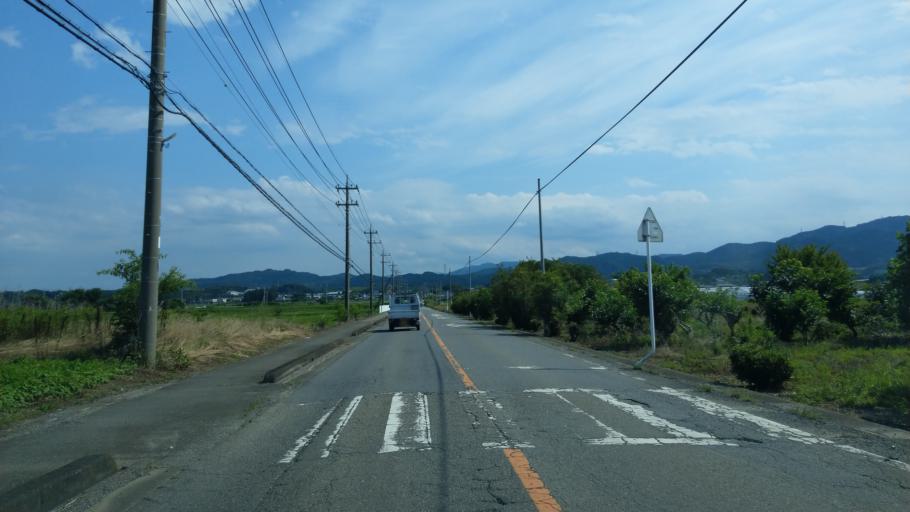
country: JP
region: Saitama
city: Kodamacho-kodamaminami
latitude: 36.1846
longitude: 139.1690
